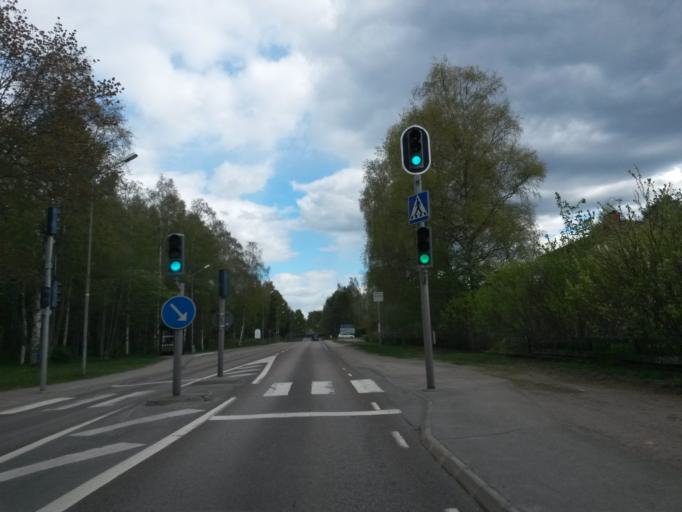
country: SE
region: Vaestra Goetaland
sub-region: Boras Kommun
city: Boras
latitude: 57.8262
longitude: 13.0028
